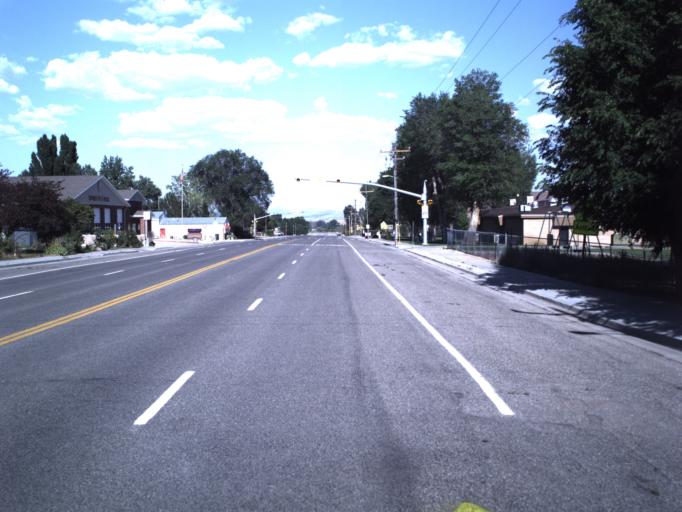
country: US
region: Utah
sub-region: Emery County
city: Huntington
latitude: 39.3486
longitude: -110.8559
